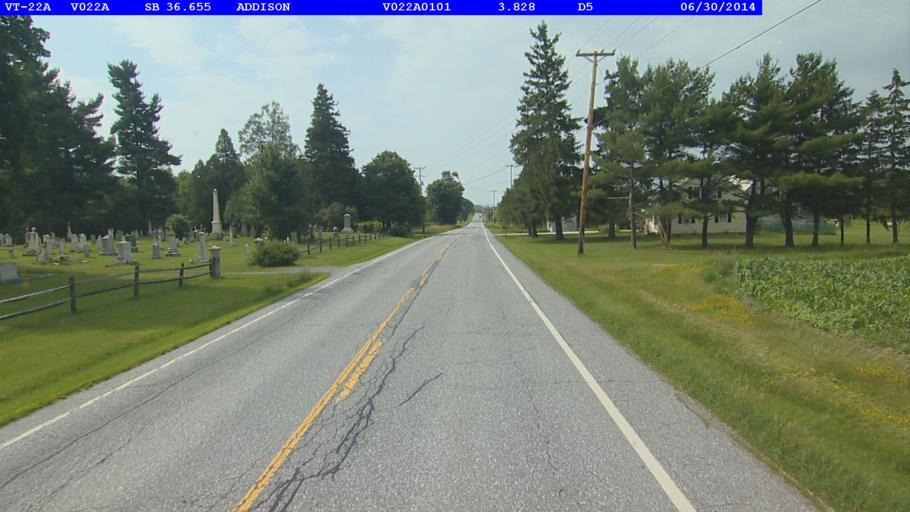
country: US
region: Vermont
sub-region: Addison County
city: Vergennes
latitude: 44.0846
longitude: -73.3028
